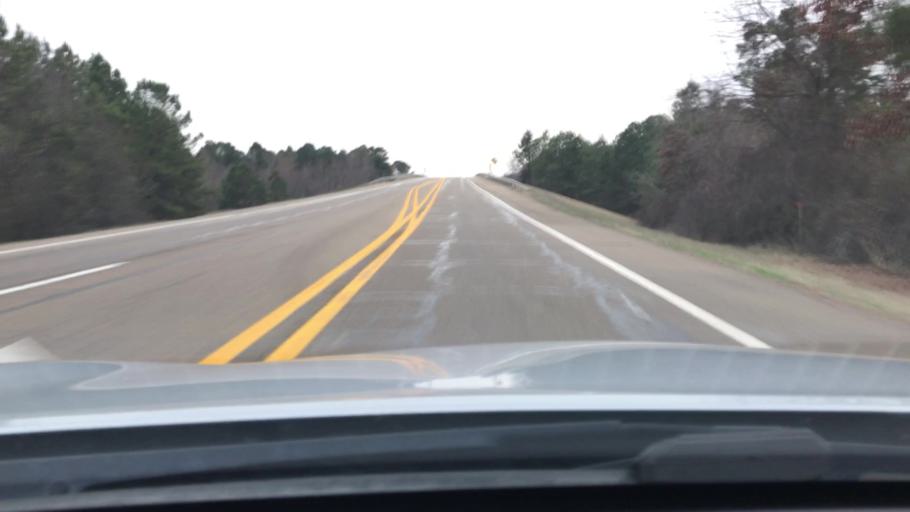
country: US
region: Arkansas
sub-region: Hempstead County
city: Hope
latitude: 33.6763
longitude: -93.5757
